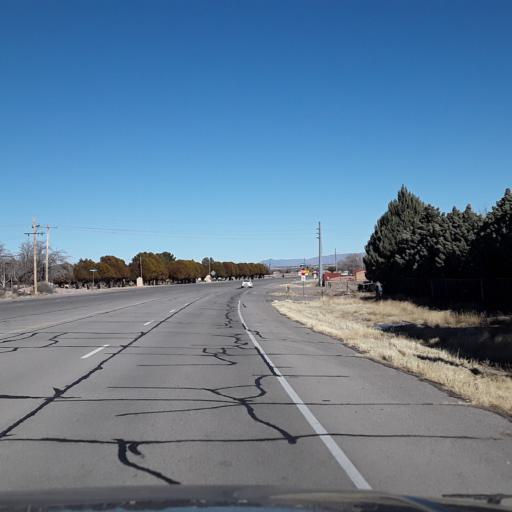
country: US
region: New Mexico
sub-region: Dona Ana County
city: Mesilla
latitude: 32.2991
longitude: -106.8545
